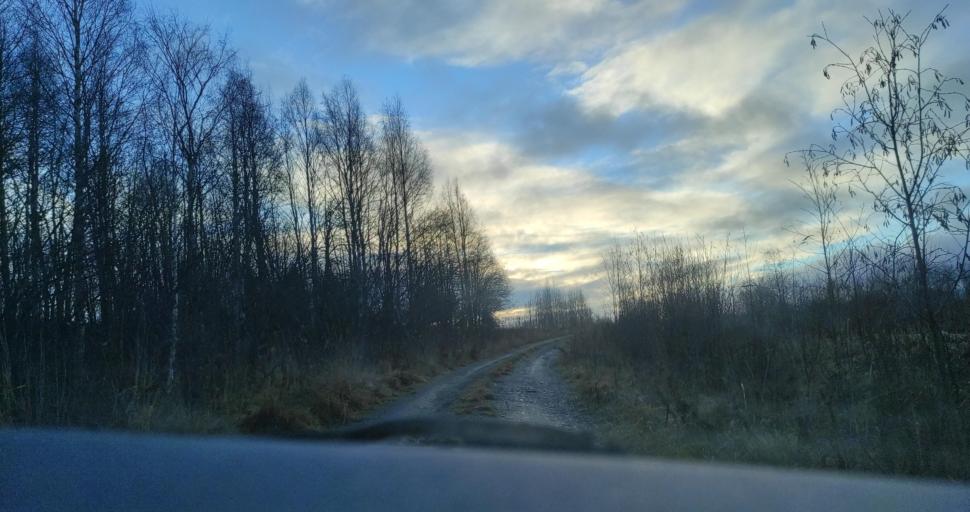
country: RU
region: Republic of Karelia
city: Pitkyaranta
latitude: 61.7285
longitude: 31.3821
